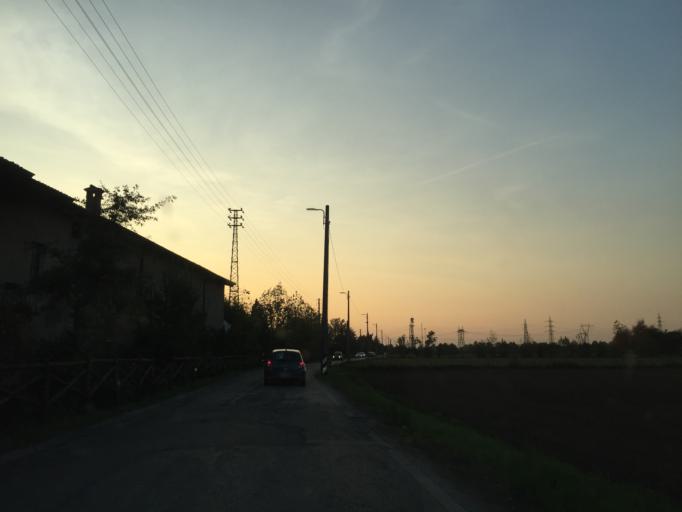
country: IT
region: Lombardy
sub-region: Provincia di Brescia
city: Folzano
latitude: 45.4912
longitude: 10.2039
